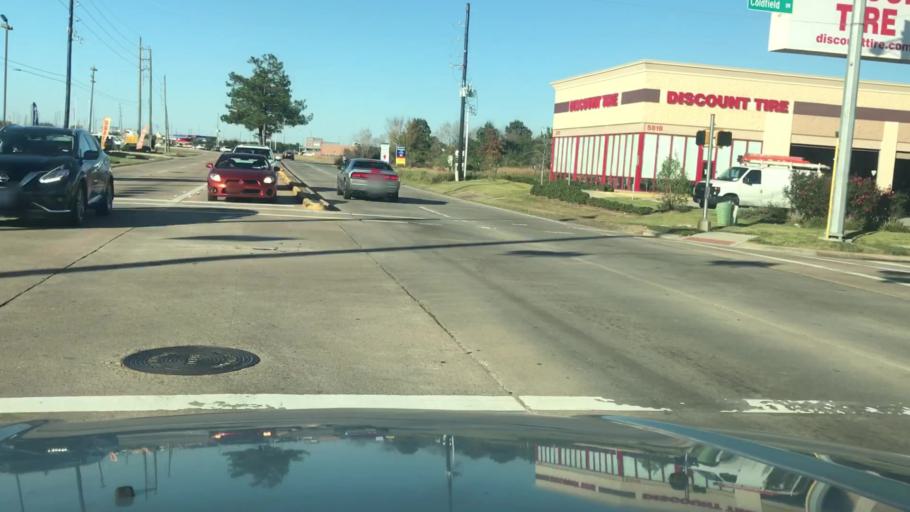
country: US
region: Texas
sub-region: Harris County
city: Cypress
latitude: 29.8549
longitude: -95.7187
